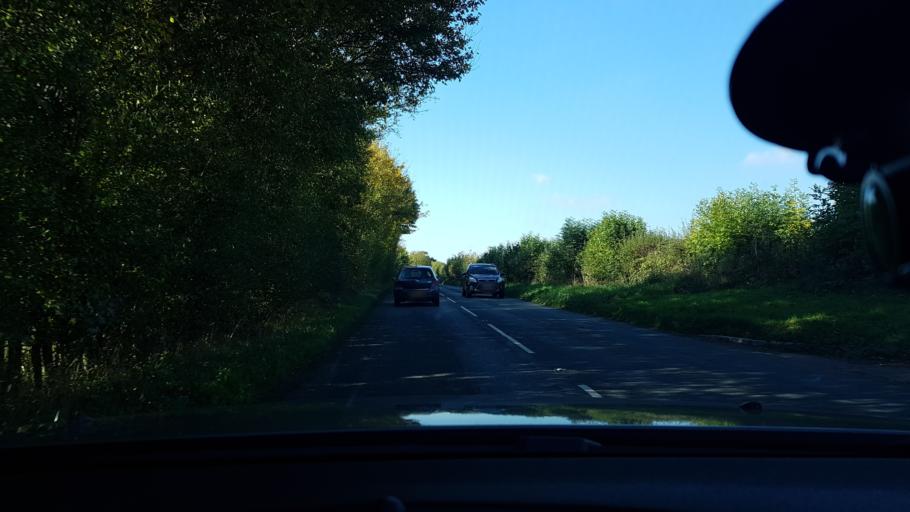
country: GB
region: England
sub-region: Wiltshire
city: Chilton Foliat
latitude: 51.4338
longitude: -1.5511
